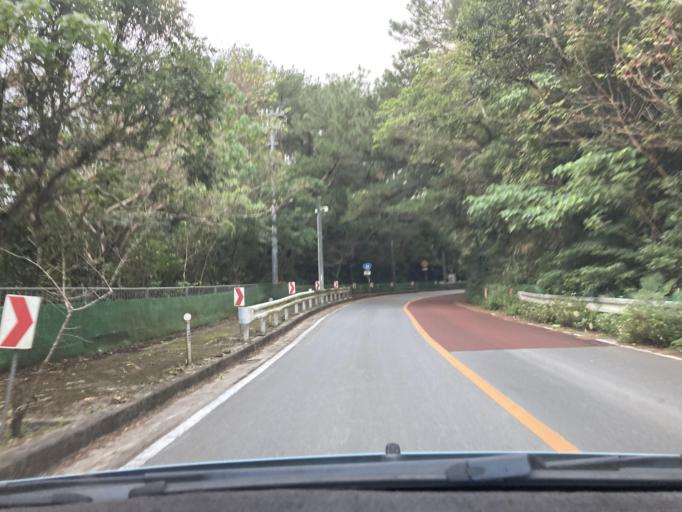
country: JP
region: Okinawa
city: Nago
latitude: 26.8313
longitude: 128.2790
